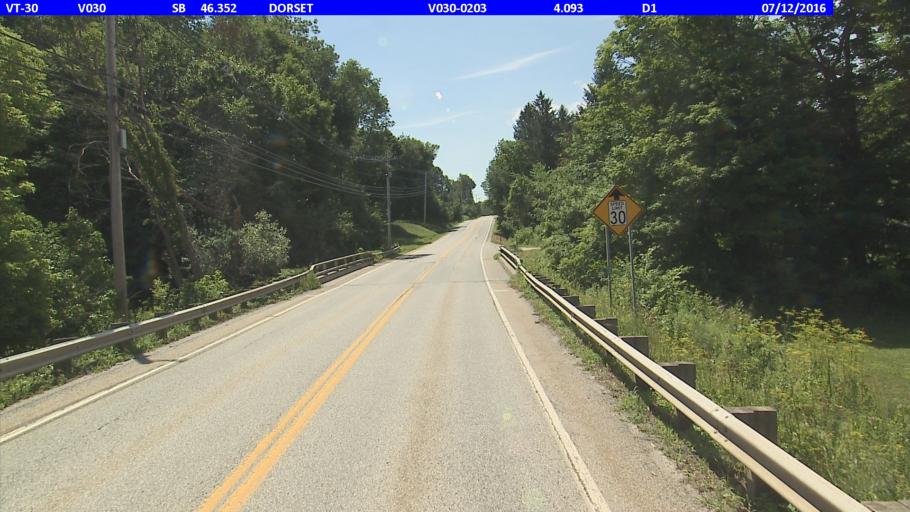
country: US
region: Vermont
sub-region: Bennington County
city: Manchester Center
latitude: 43.2640
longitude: -73.1055
